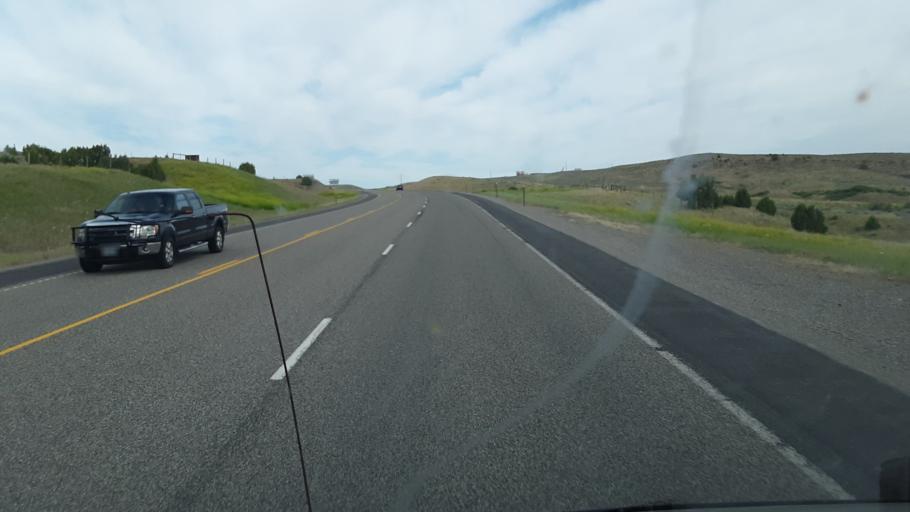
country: US
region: Wyoming
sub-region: Hot Springs County
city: Thermopolis
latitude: 43.6417
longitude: -108.2545
